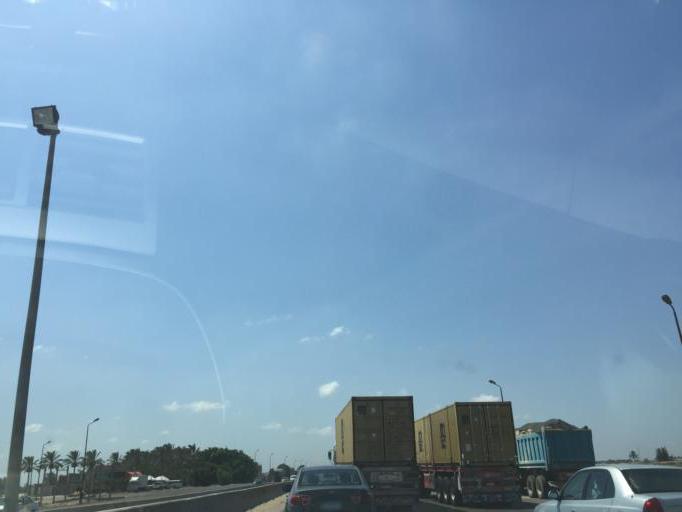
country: EG
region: Alexandria
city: Alexandria
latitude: 30.9706
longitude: 29.8263
